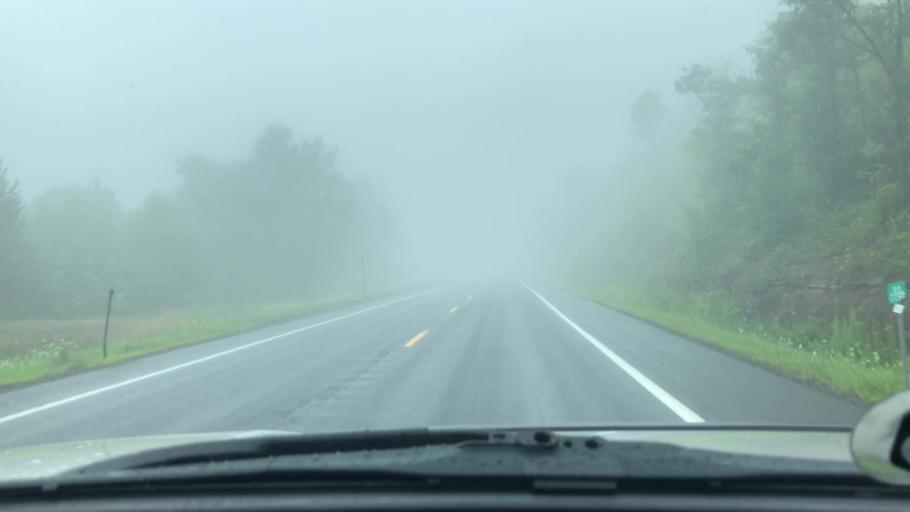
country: US
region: New York
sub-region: Greene County
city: Cairo
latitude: 42.3338
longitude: -74.1636
